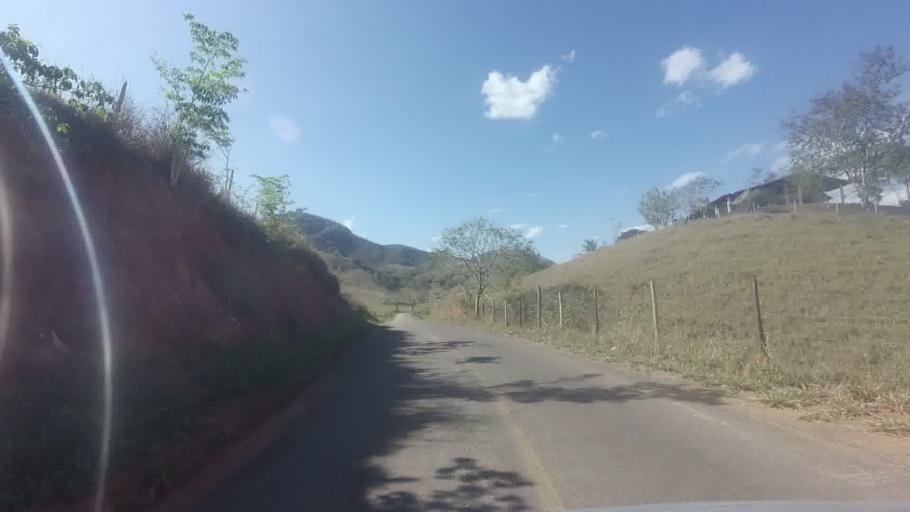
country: BR
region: Rio de Janeiro
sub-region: Bom Jesus Do Itabapoana
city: Bom Jesus do Itabapoana
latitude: -21.1180
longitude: -41.6531
